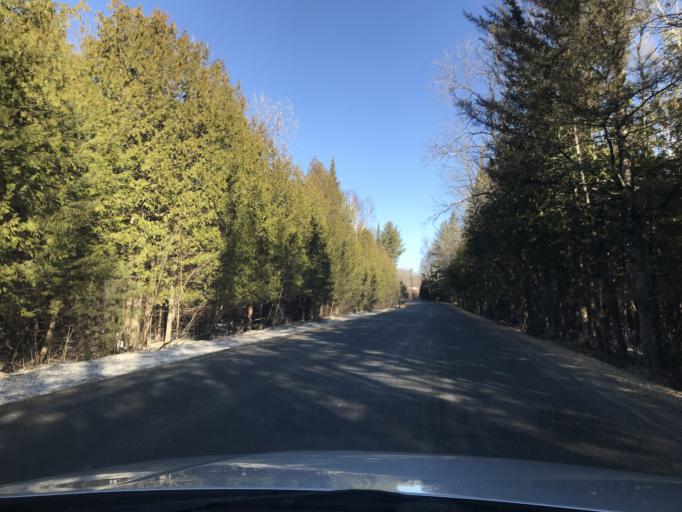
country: US
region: Wisconsin
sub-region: Marinette County
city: Niagara
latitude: 45.3779
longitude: -88.0243
